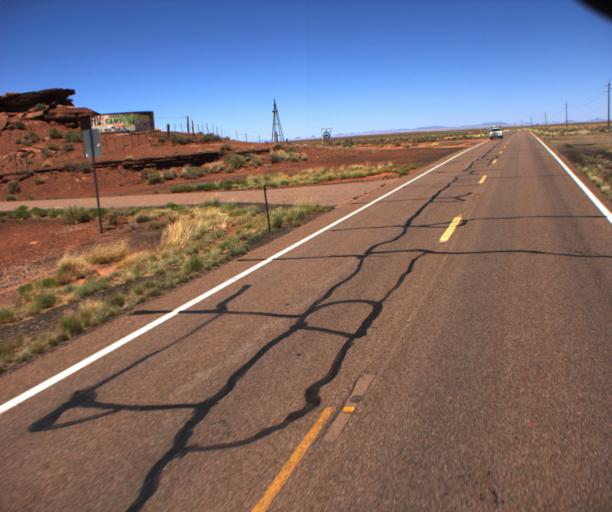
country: US
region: Arizona
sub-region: Coconino County
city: LeChee
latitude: 34.9290
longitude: -110.8013
